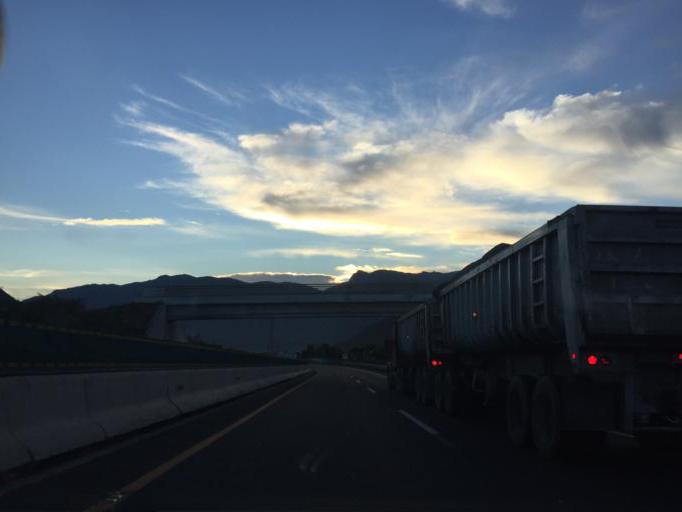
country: MX
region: Veracruz
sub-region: Nogales
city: Agricola Lazaro Cardenas
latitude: 18.8185
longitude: -97.2261
